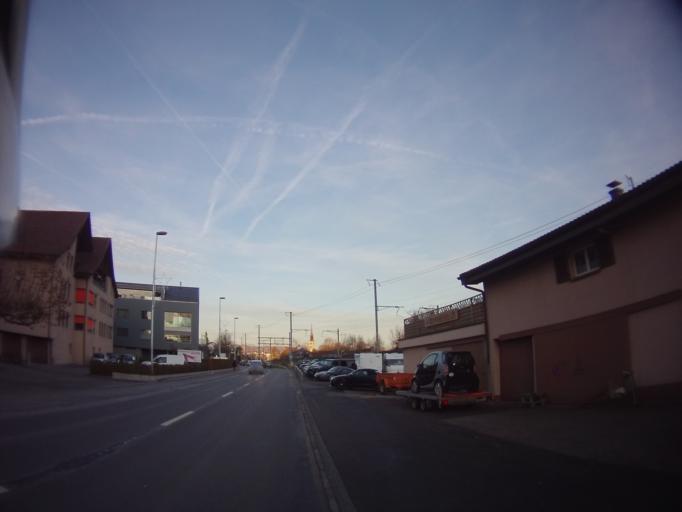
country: CH
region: Zug
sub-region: Zug
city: Cham
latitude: 47.1745
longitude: 8.4501
